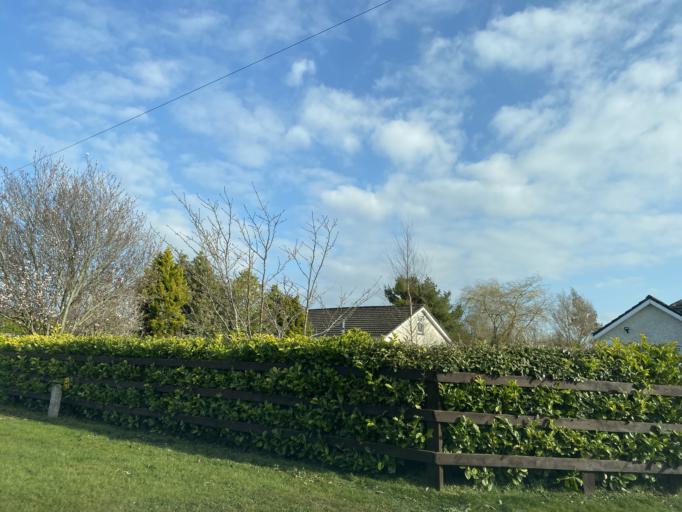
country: IE
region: Leinster
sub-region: Kildare
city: Celbridge
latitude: 53.3521
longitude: -6.5594
